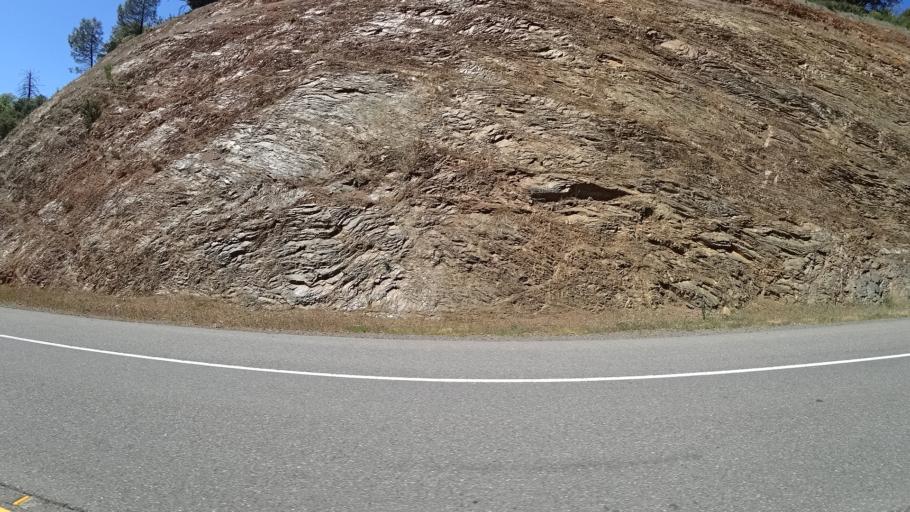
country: US
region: California
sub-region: Trinity County
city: Weaverville
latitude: 40.7357
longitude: -123.0143
